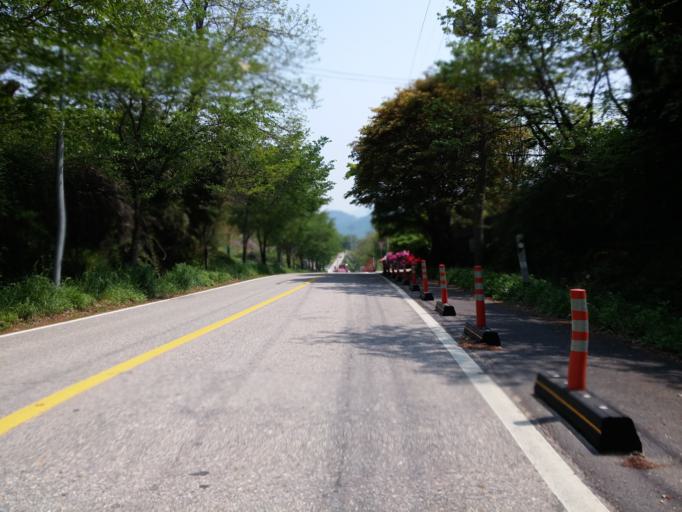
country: KR
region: Daejeon
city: Sintansin
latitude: 36.4304
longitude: 127.5400
